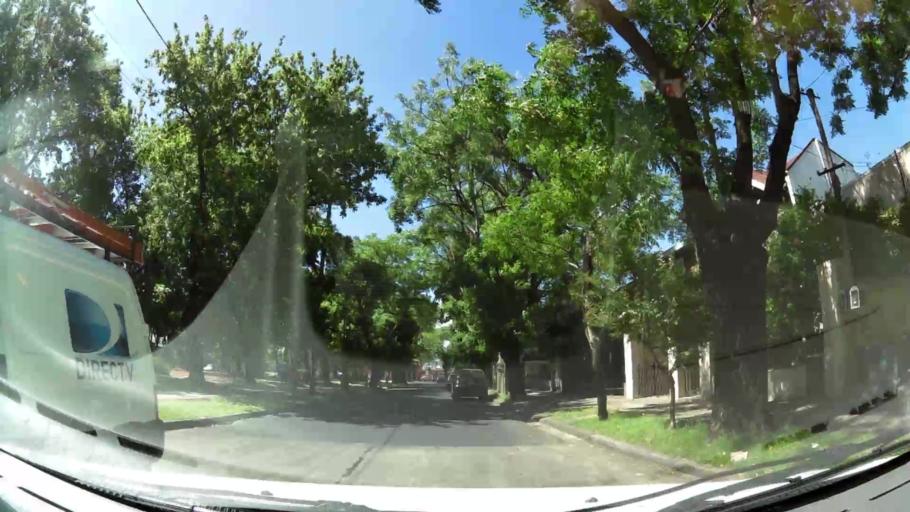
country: AR
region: Buenos Aires
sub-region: Partido de General San Martin
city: General San Martin
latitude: -34.5627
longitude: -58.5498
